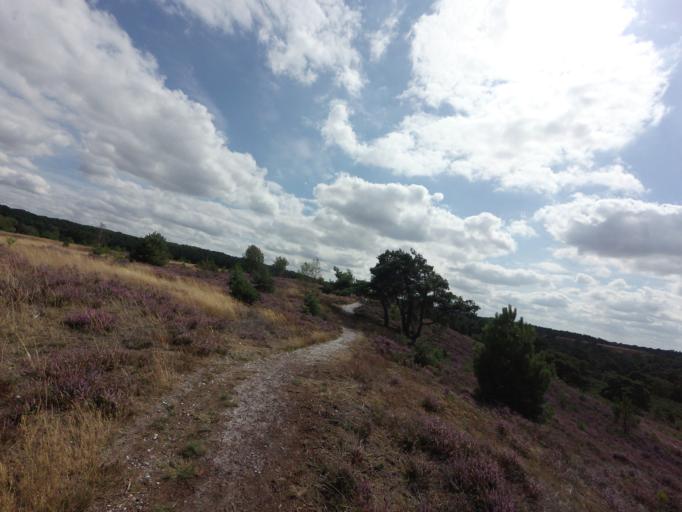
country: NL
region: Limburg
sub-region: Gemeente Brunssum
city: Brunssum
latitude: 50.9260
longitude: 6.0063
